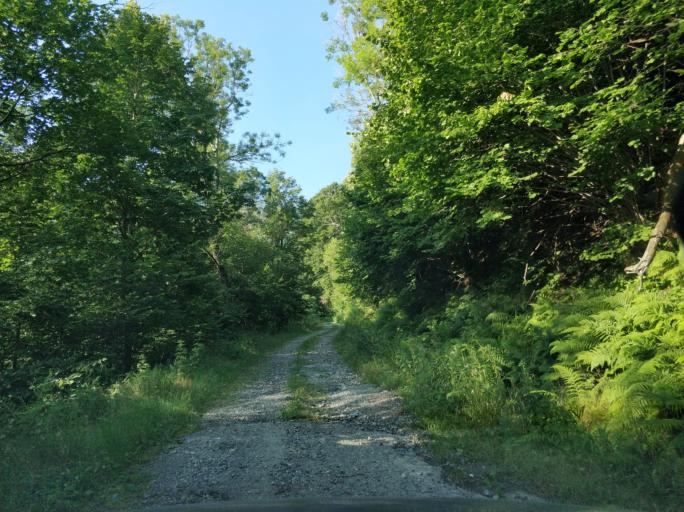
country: IT
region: Piedmont
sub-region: Provincia di Torino
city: Ceres
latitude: 45.3093
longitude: 7.3663
